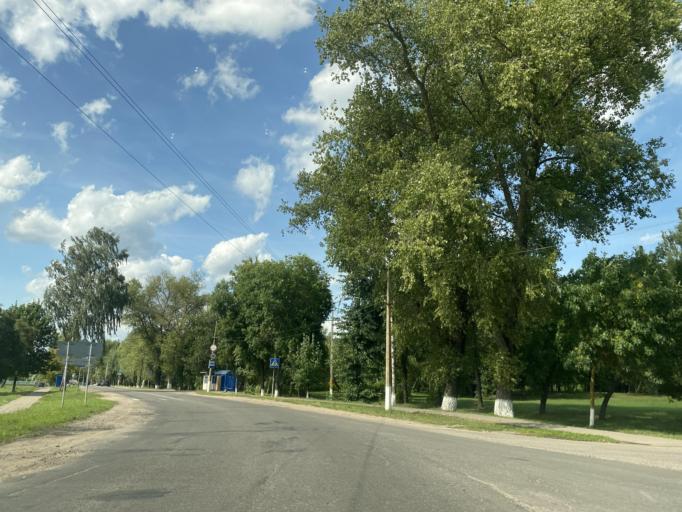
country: BY
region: Minsk
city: Horad Zhodzina
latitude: 54.0976
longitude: 28.3550
